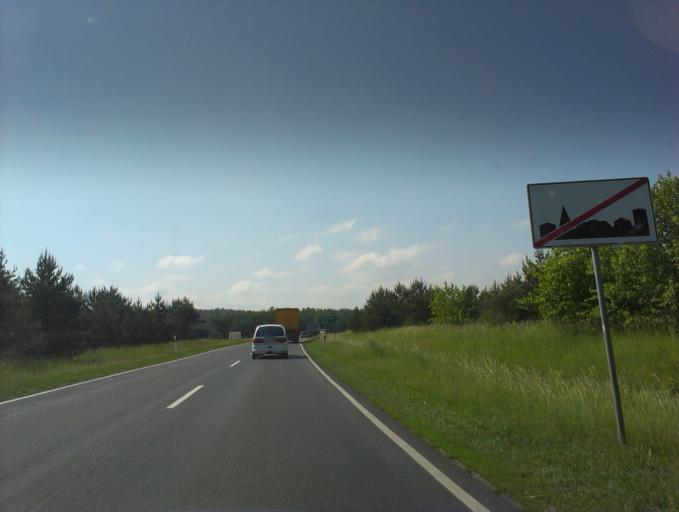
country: PL
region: Greater Poland Voivodeship
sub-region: Powiat zlotowski
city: Okonek
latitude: 53.5321
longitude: 16.8544
